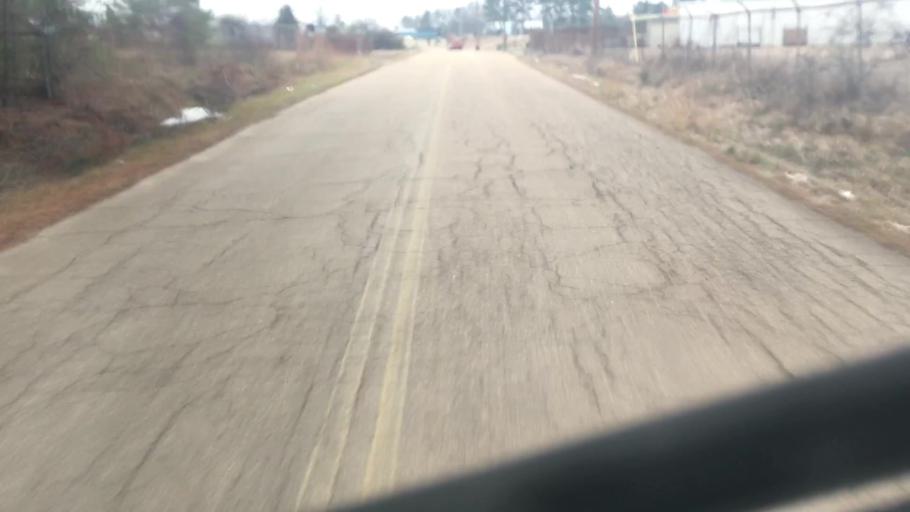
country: US
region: Alabama
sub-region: Walker County
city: Jasper
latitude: 33.8344
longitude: -87.2254
